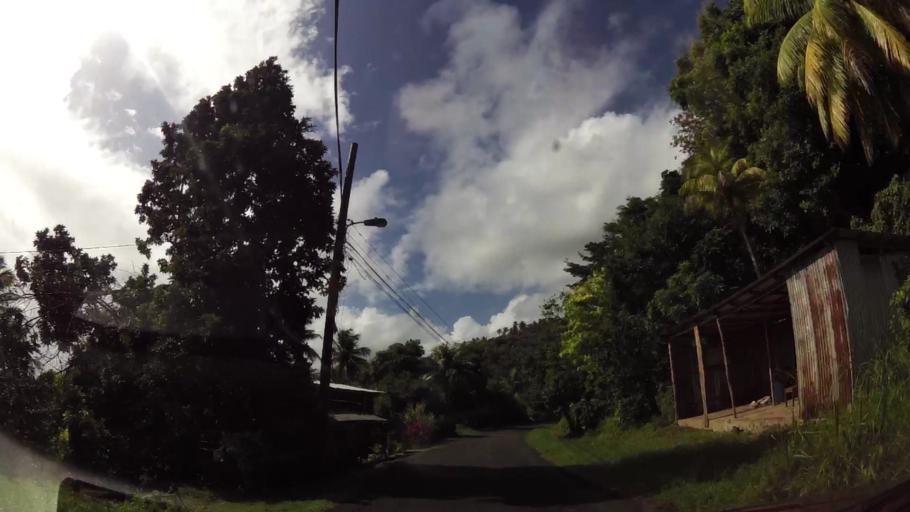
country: DM
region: Saint David
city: Castle Bruce
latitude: 15.4721
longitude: -61.2475
